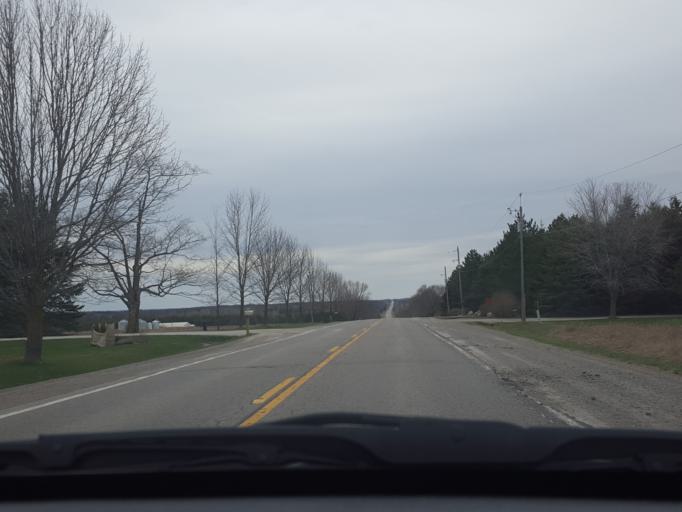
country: CA
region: Ontario
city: Uxbridge
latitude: 44.2780
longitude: -79.1625
